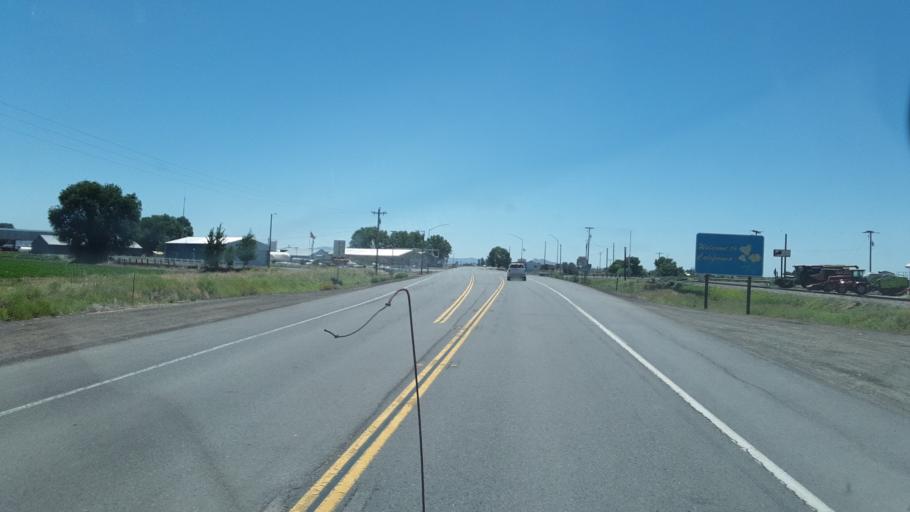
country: US
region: California
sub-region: Siskiyou County
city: Tulelake
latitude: 41.9997
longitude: -121.5213
